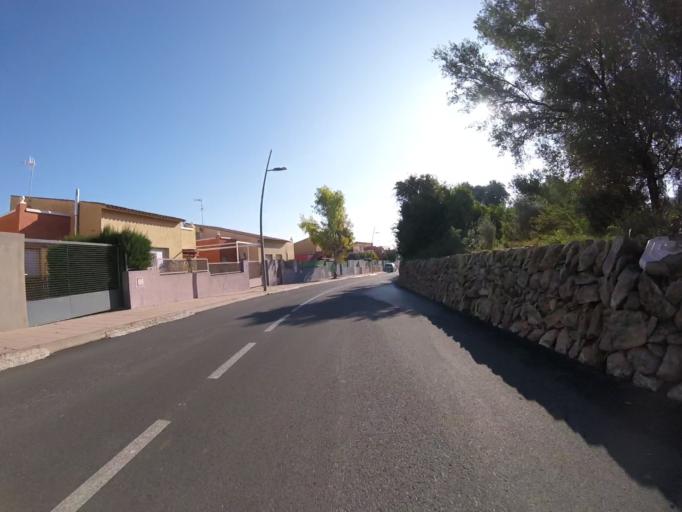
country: ES
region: Valencia
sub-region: Provincia de Castello
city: Peniscola
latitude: 40.3884
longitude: 0.3764
